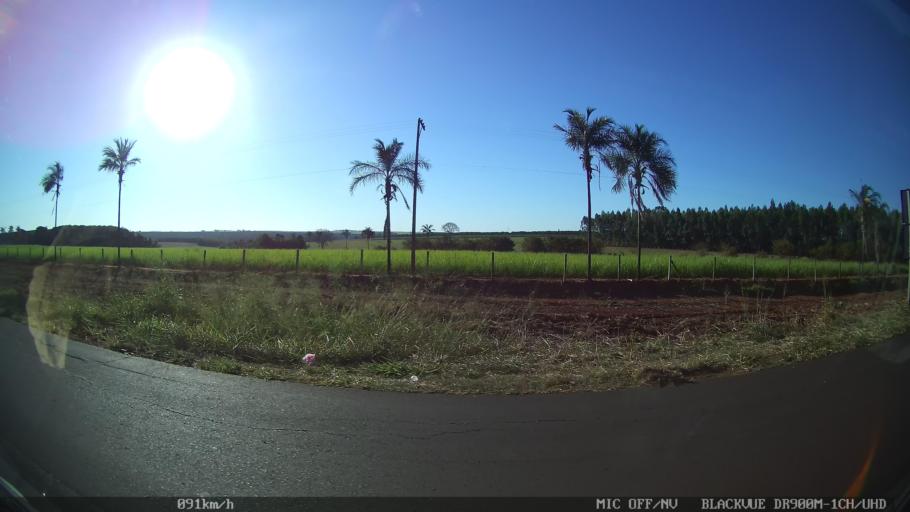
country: BR
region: Sao Paulo
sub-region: Guapiacu
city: Guapiacu
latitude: -20.7501
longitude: -49.1335
